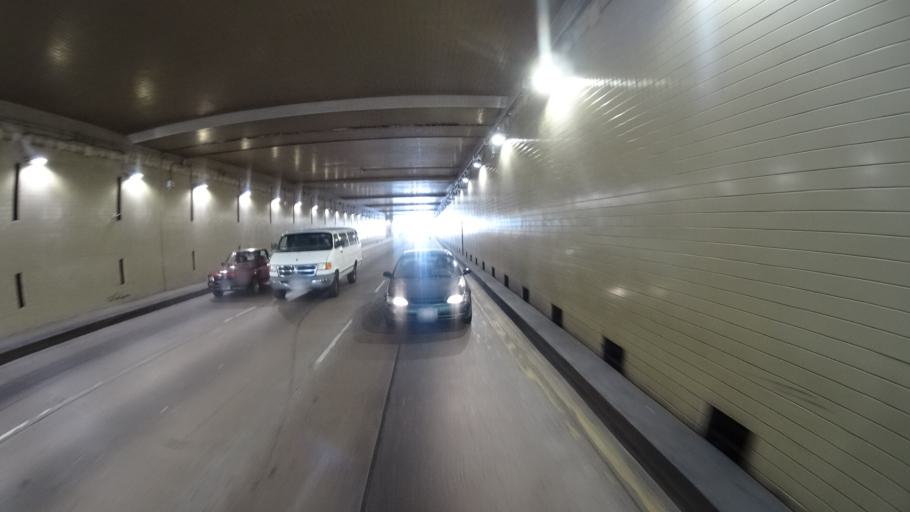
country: US
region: California
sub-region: Los Angeles County
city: Van Nuys
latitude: 34.2012
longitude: -118.4899
